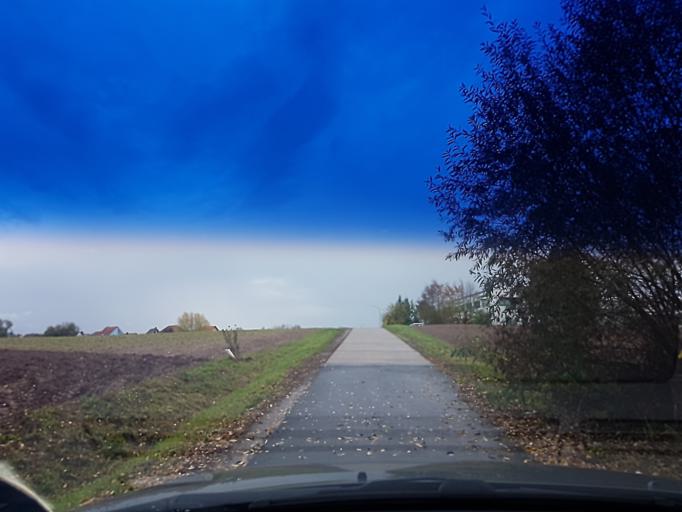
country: DE
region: Bavaria
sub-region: Upper Franconia
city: Schlusselfeld
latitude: 49.7576
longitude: 10.6292
